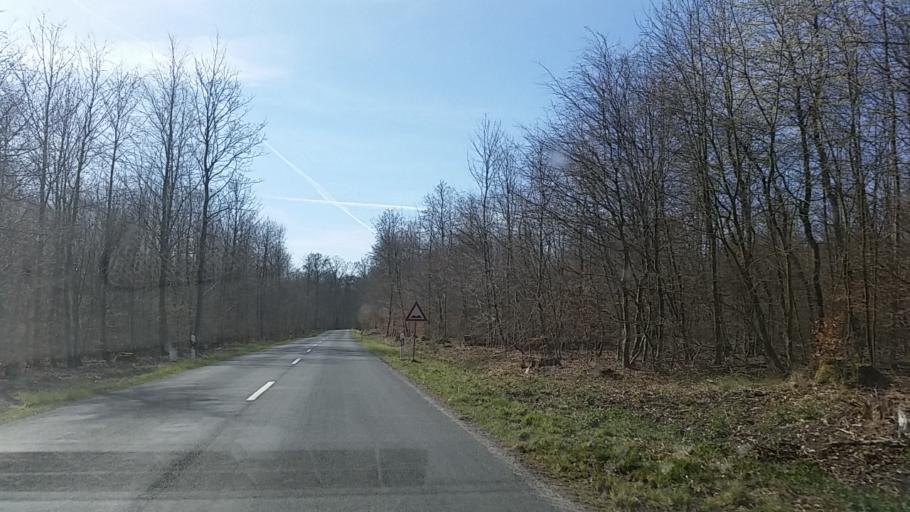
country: DE
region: Lower Saxony
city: Rabke
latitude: 52.1865
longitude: 10.8420
